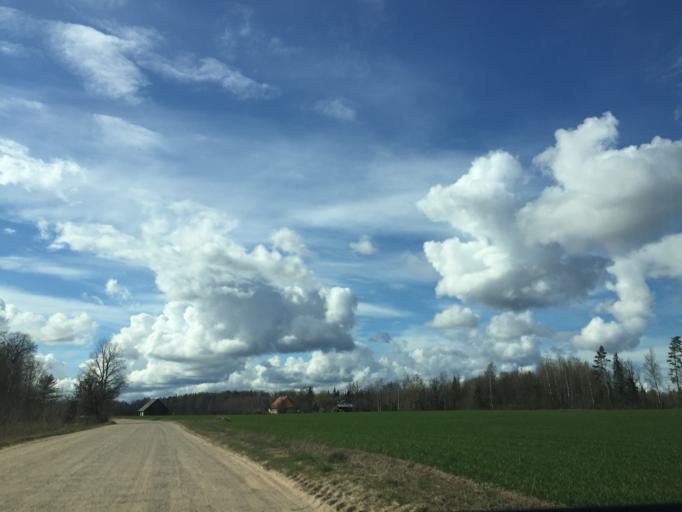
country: LV
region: Burtnieki
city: Matisi
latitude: 57.5984
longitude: 25.0703
